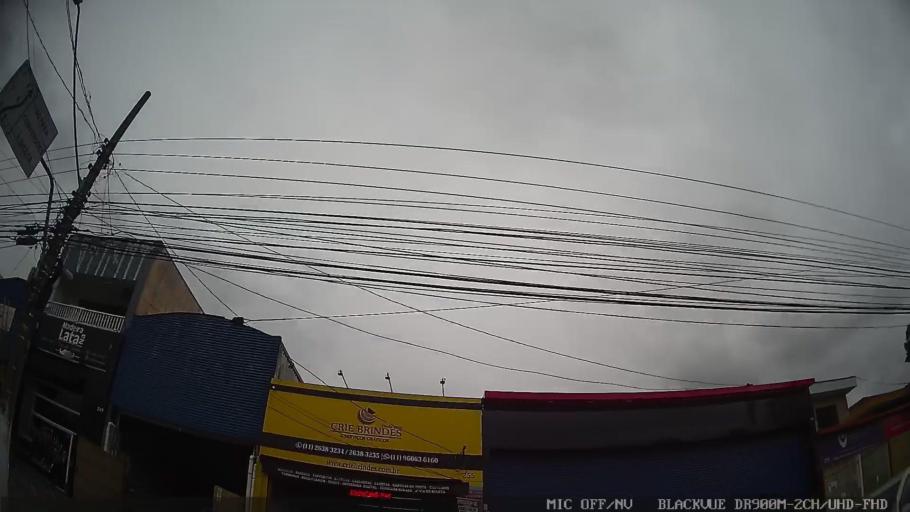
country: BR
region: Sao Paulo
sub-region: Osasco
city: Osasco
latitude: -23.5050
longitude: -46.7480
